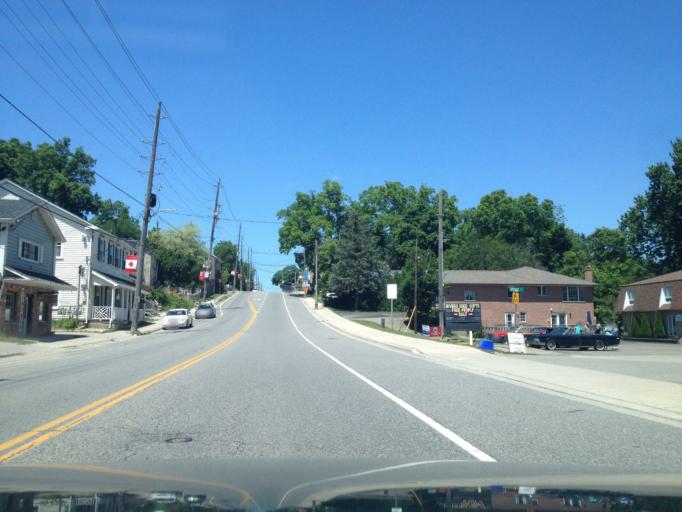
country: CA
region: Ontario
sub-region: Wellington County
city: Guelph
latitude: 43.6171
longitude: -80.1418
